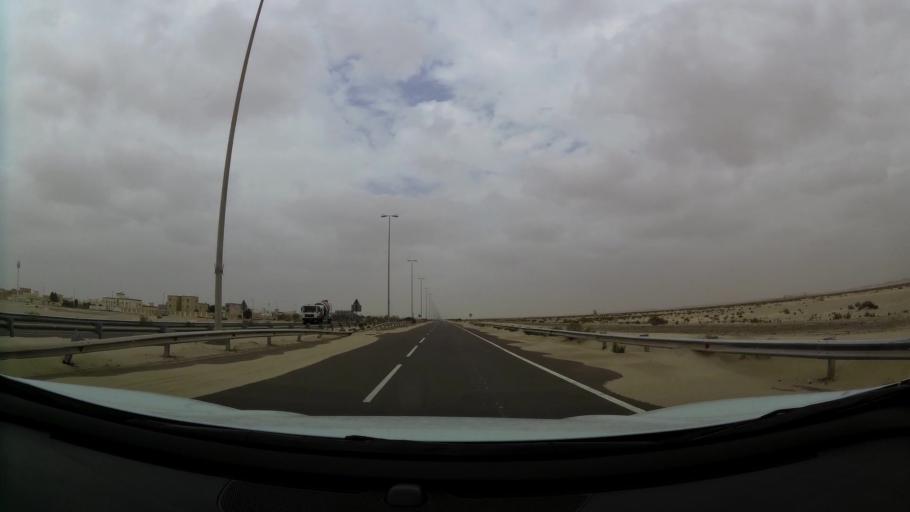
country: AE
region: Abu Dhabi
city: Abu Dhabi
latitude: 24.3323
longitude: 54.6494
